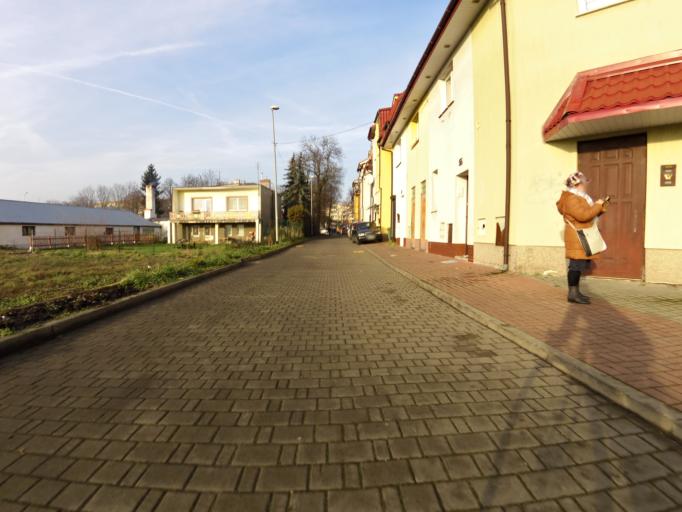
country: PL
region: West Pomeranian Voivodeship
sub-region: Powiat mysliborski
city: Debno
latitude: 52.7342
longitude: 14.6988
